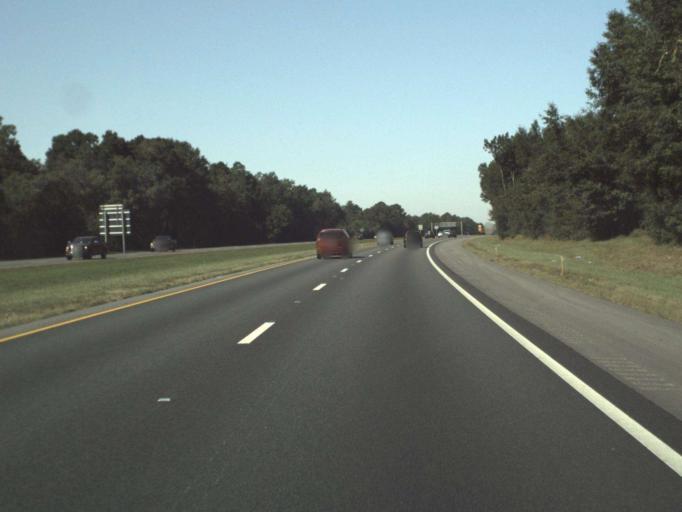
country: US
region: Florida
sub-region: Escambia County
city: Ensley
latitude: 30.5055
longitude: -87.2829
